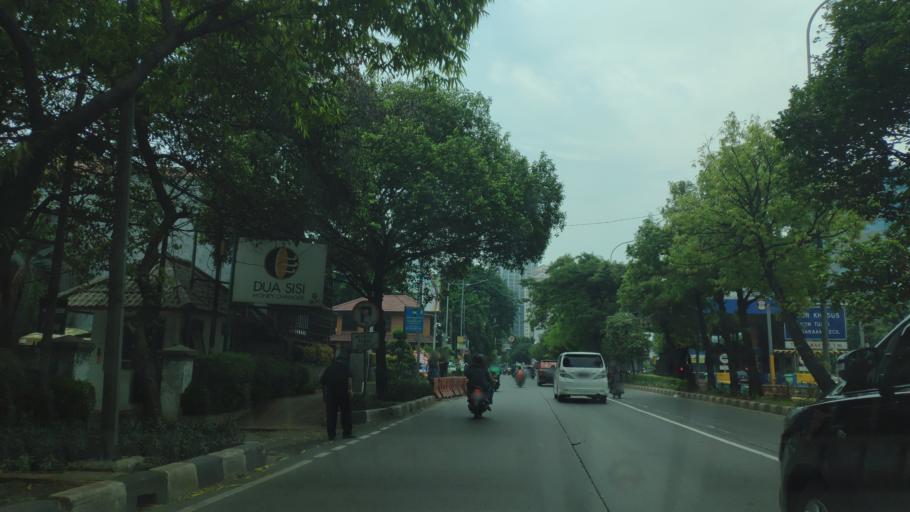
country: ID
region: Jakarta Raya
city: Jakarta
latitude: -6.1946
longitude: 106.7976
